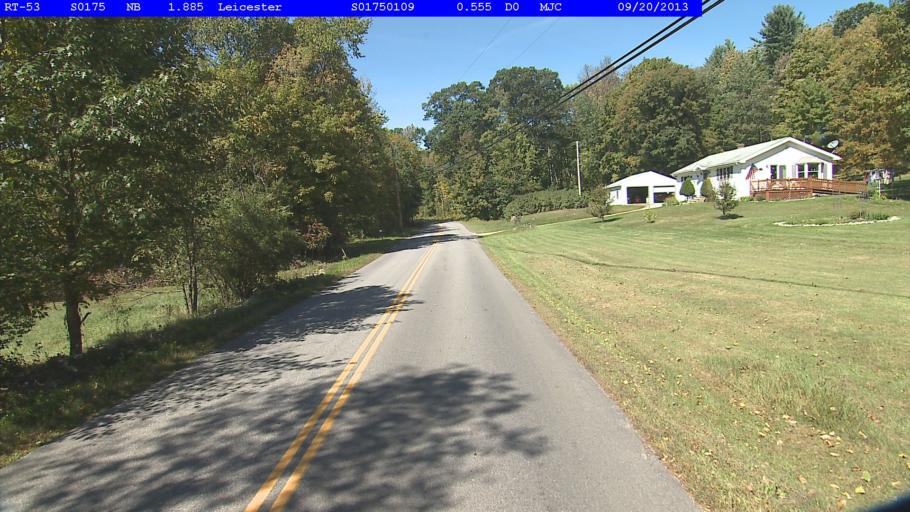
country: US
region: Vermont
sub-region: Rutland County
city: Brandon
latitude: 43.8532
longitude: -73.0617
